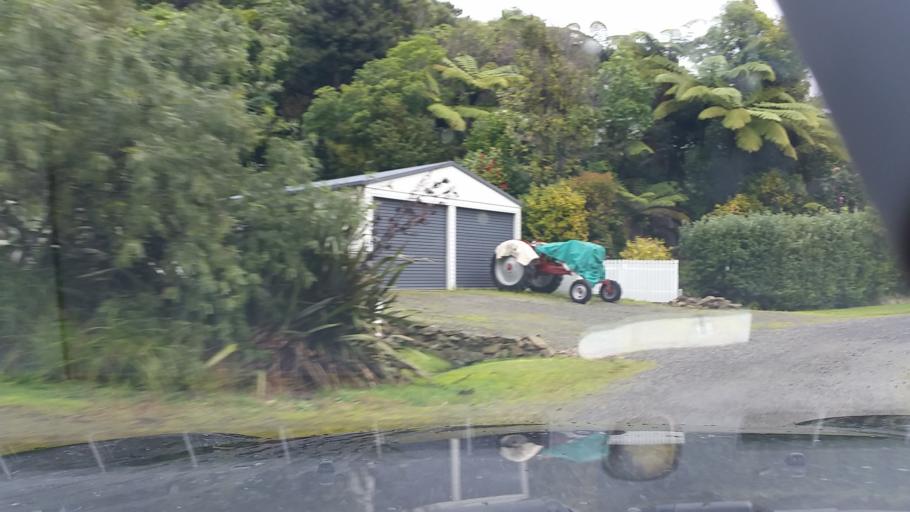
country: NZ
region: Marlborough
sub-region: Marlborough District
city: Picton
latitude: -41.2700
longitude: 174.0788
